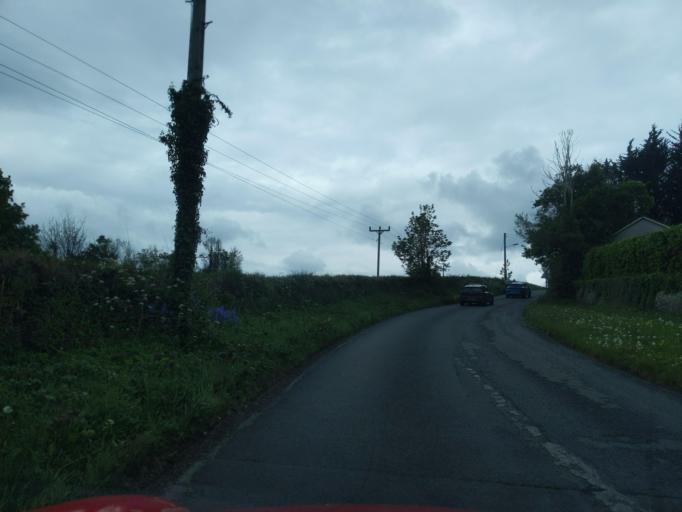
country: GB
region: England
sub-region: Cornwall
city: Saltash
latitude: 50.4154
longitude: -4.2165
